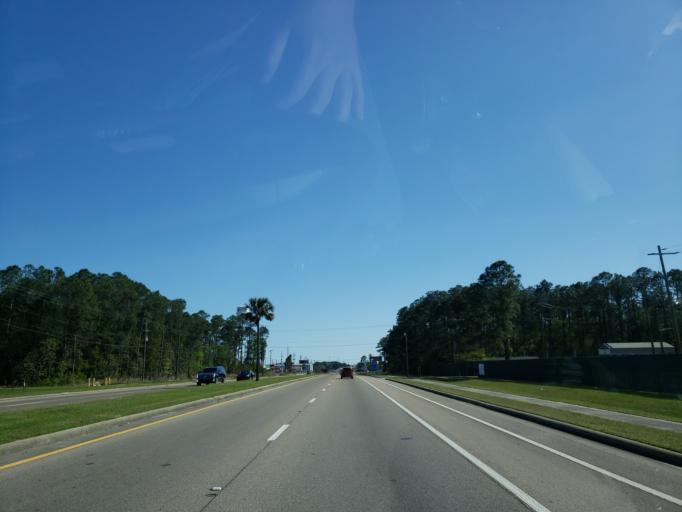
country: US
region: Mississippi
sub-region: Harrison County
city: West Gulfport
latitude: 30.4378
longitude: -89.0313
